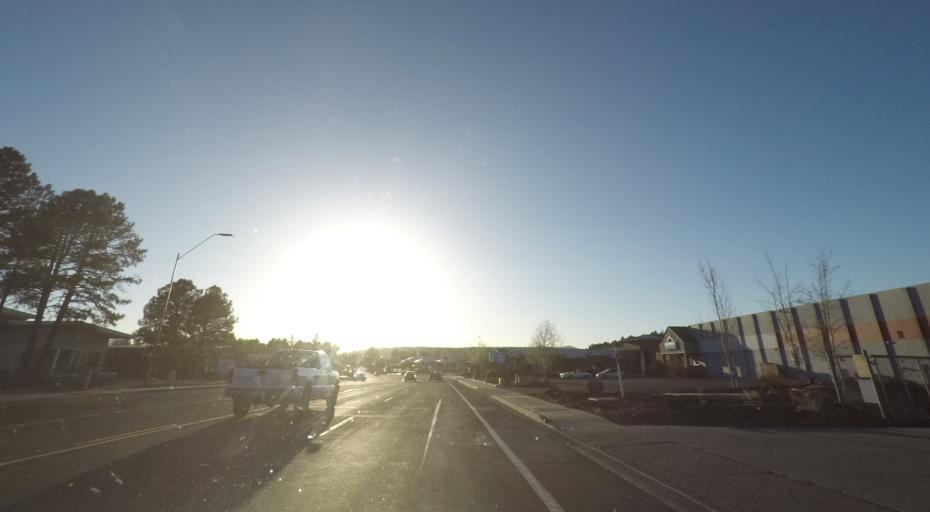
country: US
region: Arizona
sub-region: Coconino County
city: Flagstaff
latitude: 35.1914
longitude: -111.6334
